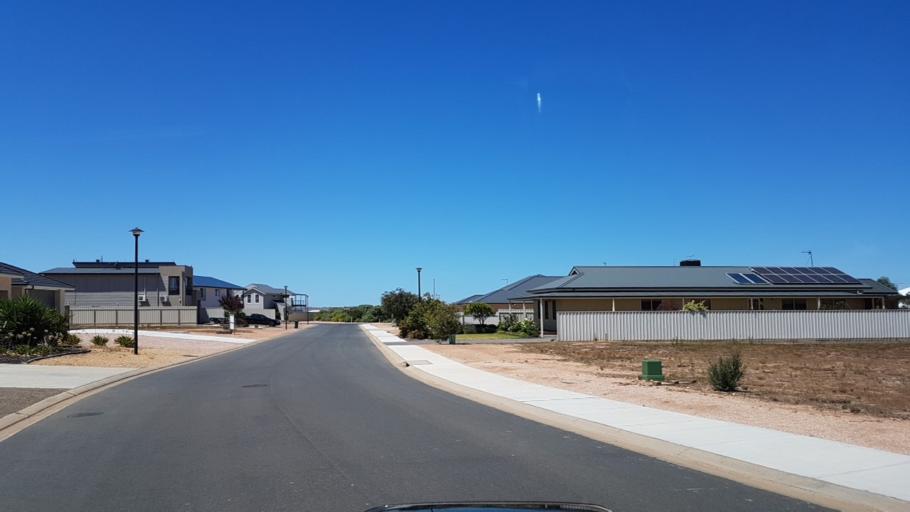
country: AU
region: South Australia
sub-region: Copper Coast
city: Wallaroo
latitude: -33.8938
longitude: 137.6296
